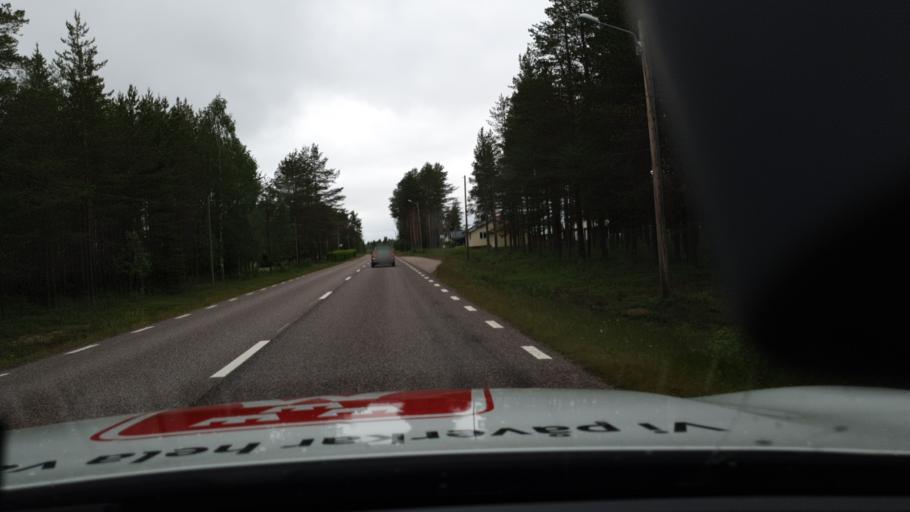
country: FI
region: Lapland
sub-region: Torniolaakso
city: Pello
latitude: 66.9775
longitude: 23.8036
